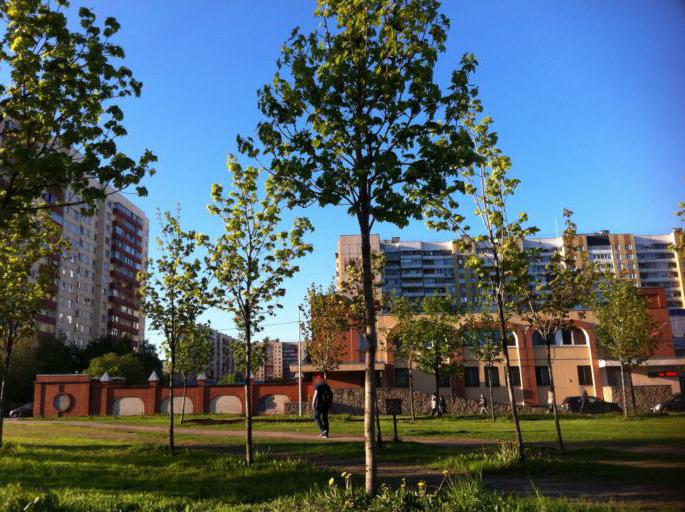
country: RU
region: St.-Petersburg
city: Dachnoye
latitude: 59.8529
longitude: 30.2169
